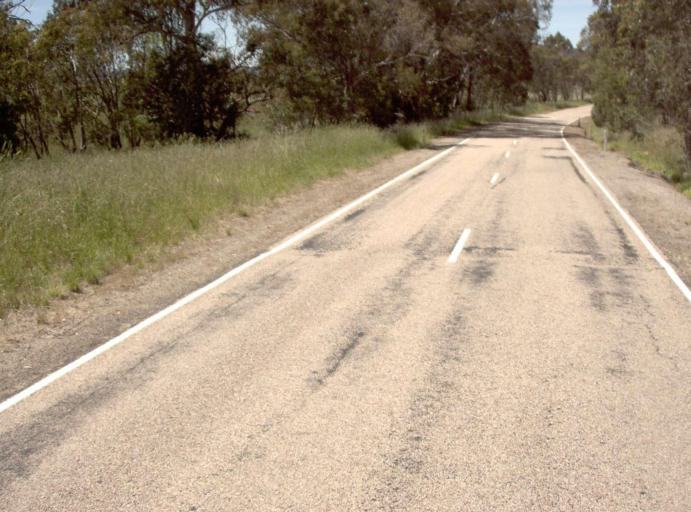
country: AU
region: Victoria
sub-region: East Gippsland
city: Lakes Entrance
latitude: -37.1737
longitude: 148.2669
